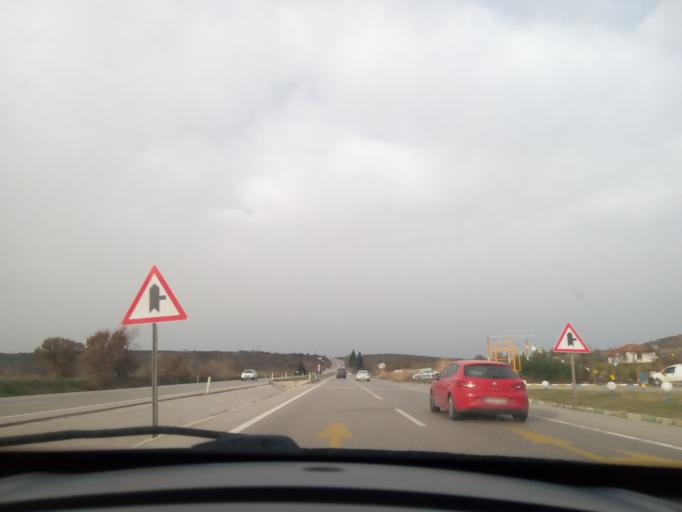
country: TR
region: Bursa
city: Mahmudiye
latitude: 40.2161
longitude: 28.6560
